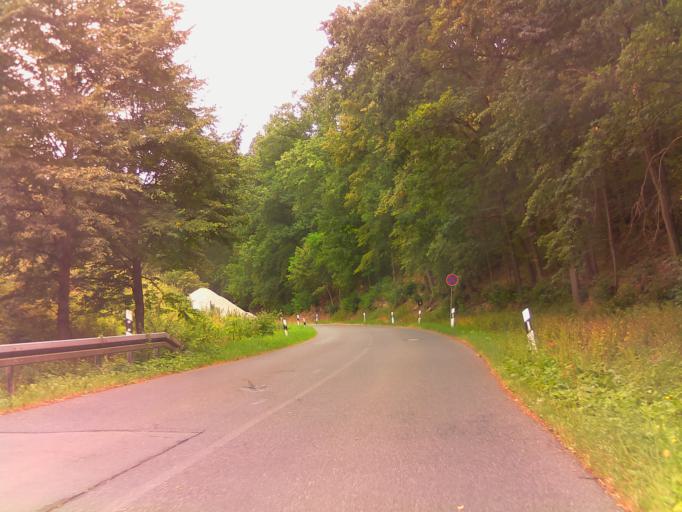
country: DE
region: Thuringia
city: Orlamunde
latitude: 50.7670
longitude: 11.5116
